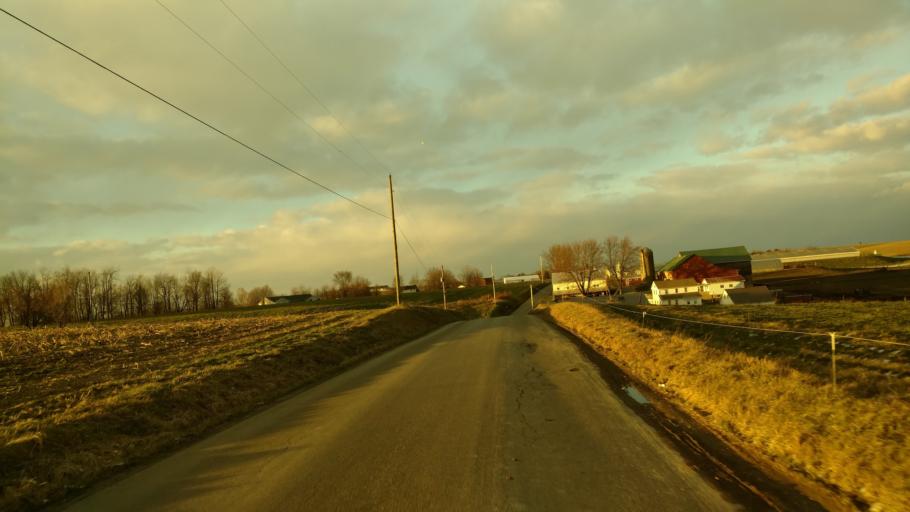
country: US
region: Ohio
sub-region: Tuscarawas County
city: Sugarcreek
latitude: 40.5180
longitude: -81.7807
